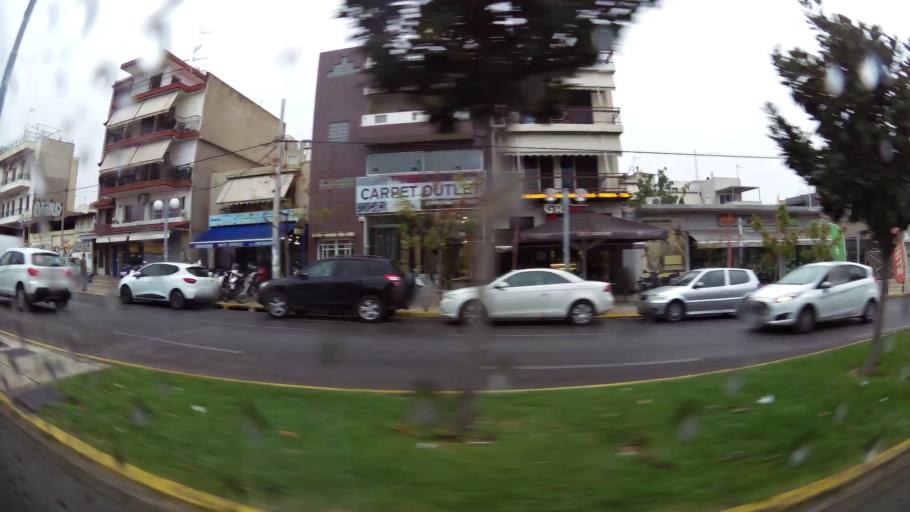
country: GR
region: Attica
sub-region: Nomarchia Athinas
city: Agia Varvara
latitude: 37.9962
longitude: 23.6699
